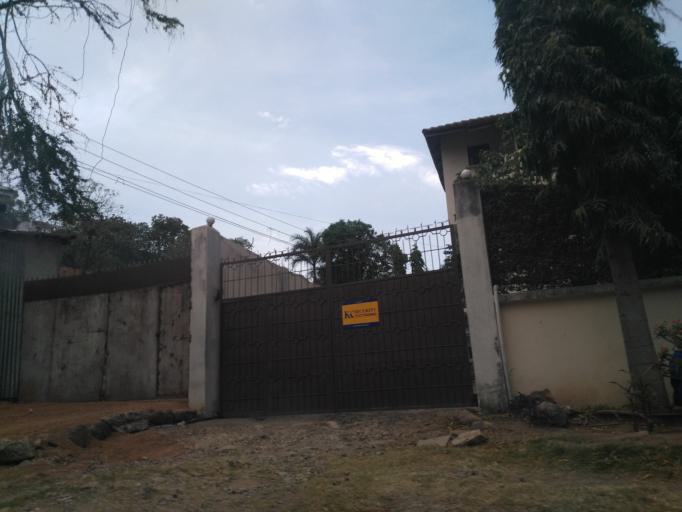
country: TZ
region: Mwanza
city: Mwanza
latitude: -2.5275
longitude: 32.8931
